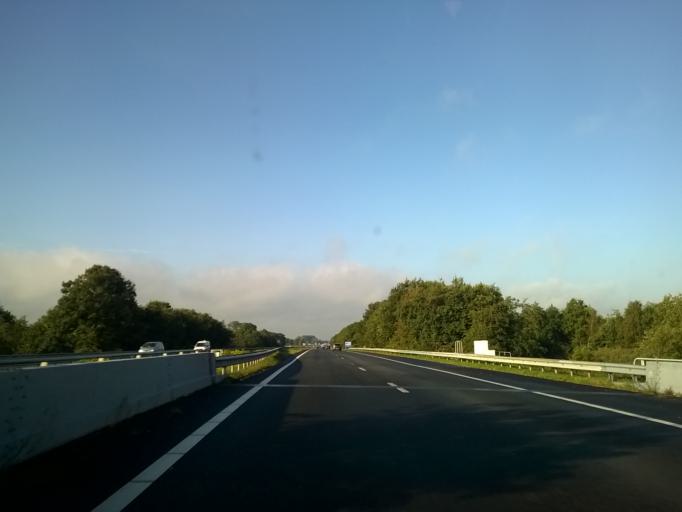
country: NL
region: Groningen
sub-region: Gemeente Leek
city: Leek
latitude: 53.1710
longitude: 6.3329
